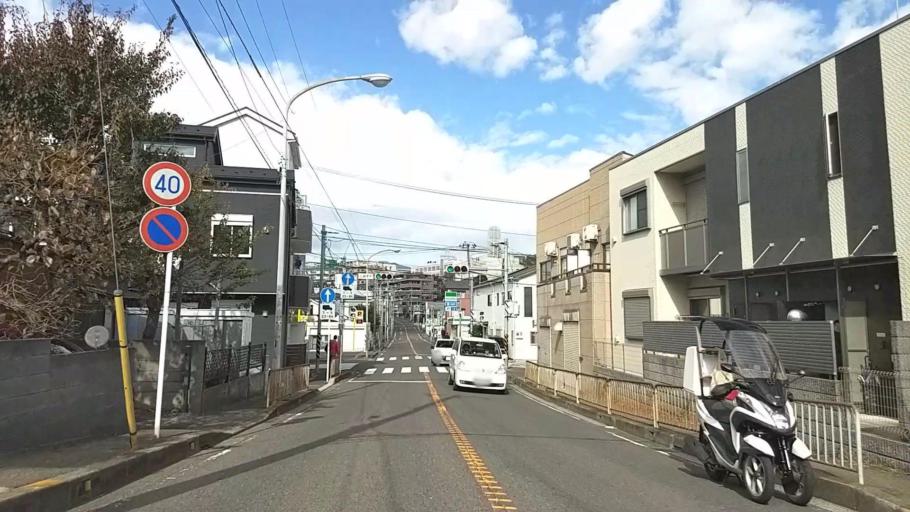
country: JP
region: Kanagawa
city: Yokohama
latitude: 35.4879
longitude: 139.6395
